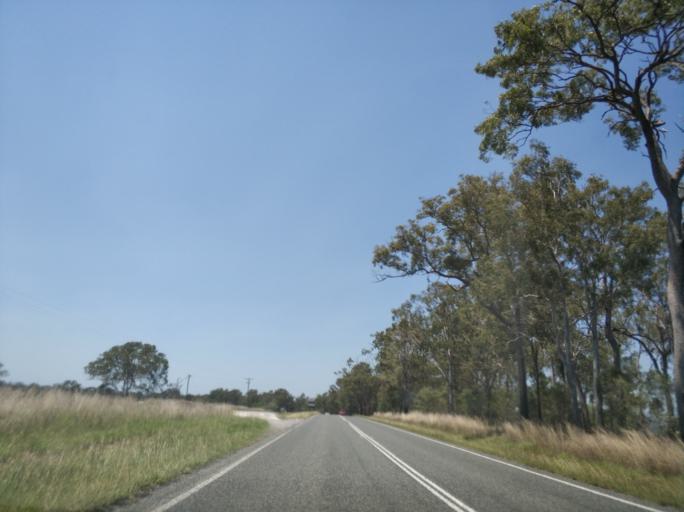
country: AU
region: Queensland
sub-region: Gladstone
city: Toolooa
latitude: -24.3292
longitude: 151.5775
